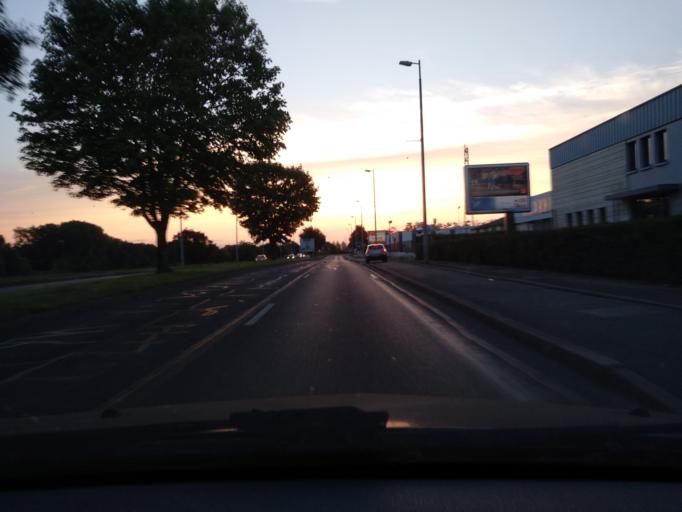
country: FR
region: Centre
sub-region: Departement d'Indre-et-Loire
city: Tours
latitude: 47.3743
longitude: 0.6747
